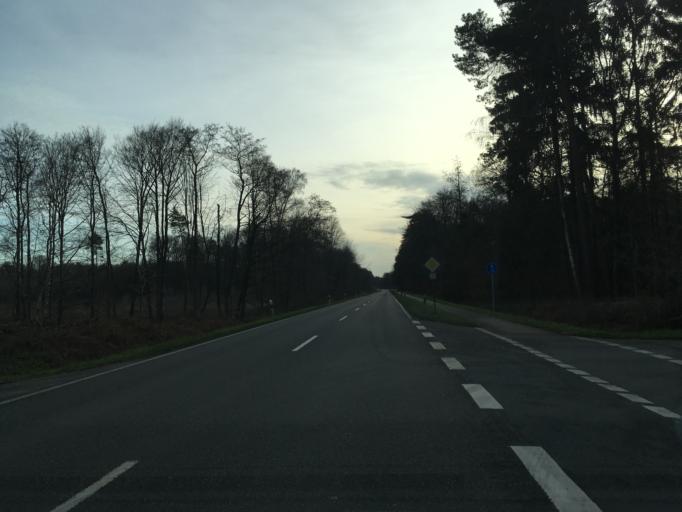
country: DE
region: North Rhine-Westphalia
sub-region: Regierungsbezirk Munster
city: Ahaus
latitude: 52.0354
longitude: 7.0236
